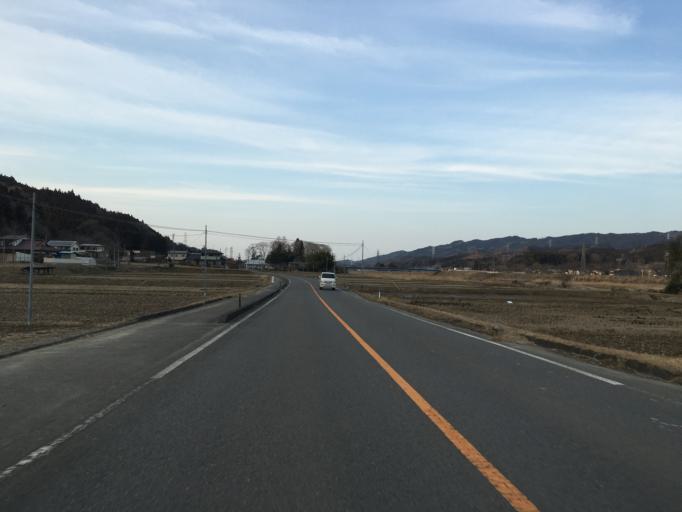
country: JP
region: Ibaraki
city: Daigo
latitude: 36.8720
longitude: 140.4159
